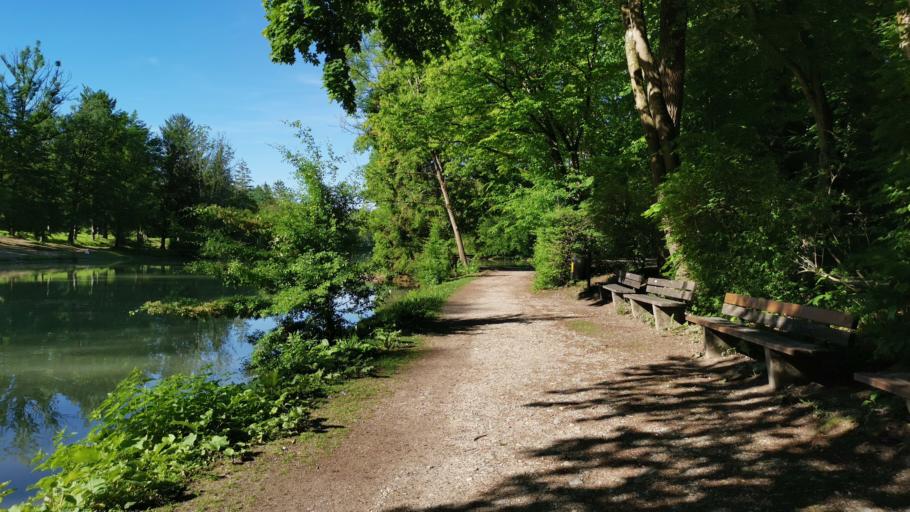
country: DE
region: Bavaria
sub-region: Upper Bavaria
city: Pullach im Isartal
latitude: 48.0872
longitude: 11.5437
